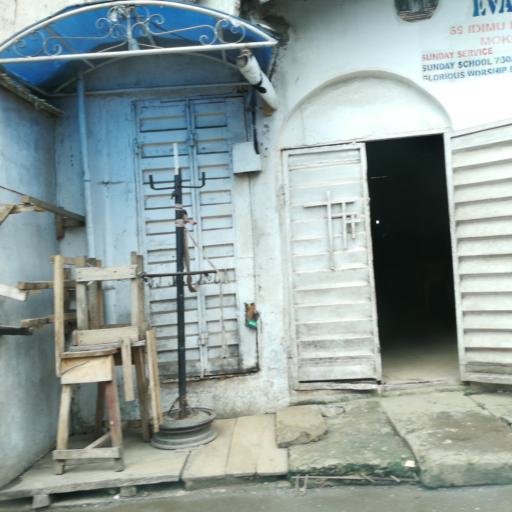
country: NG
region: Lagos
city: Agege
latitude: 6.6003
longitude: 3.2920
